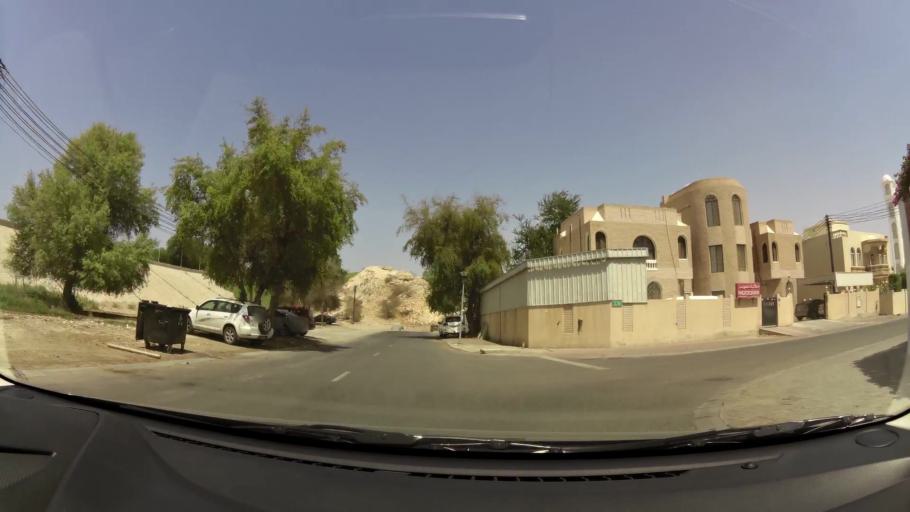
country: OM
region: Muhafazat Masqat
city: Muscat
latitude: 23.6155
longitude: 58.4992
